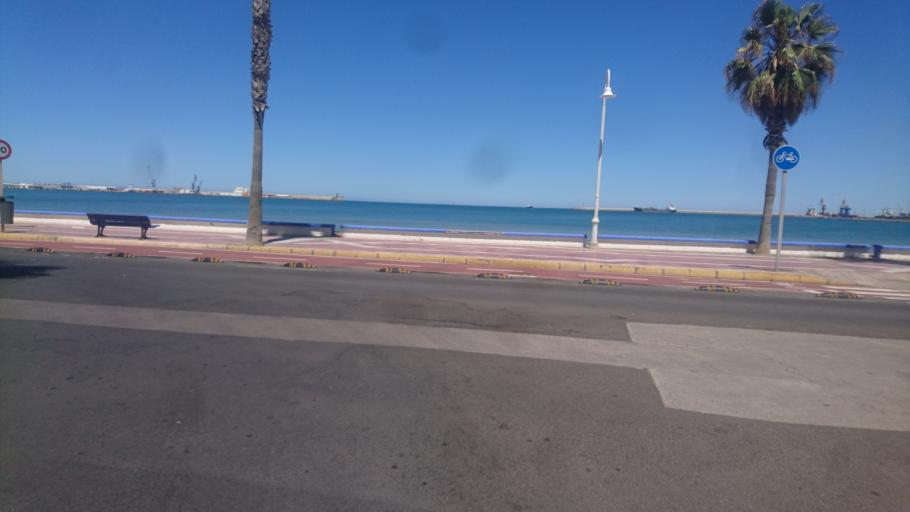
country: ES
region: Melilla
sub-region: Melilla
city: Melilla
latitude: 35.2784
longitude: -2.9359
